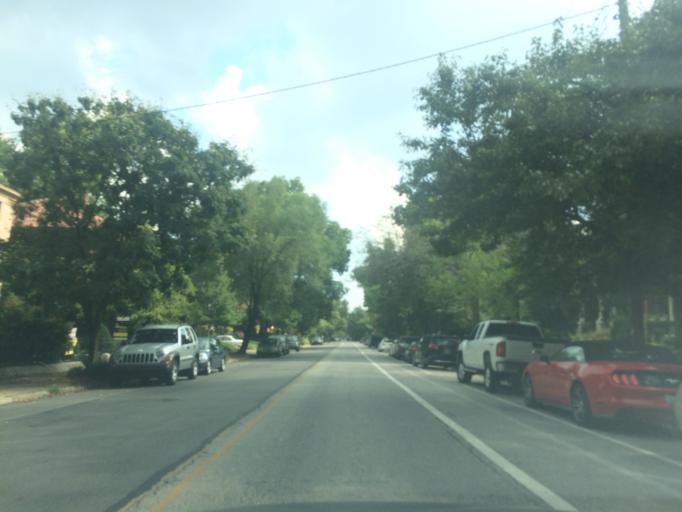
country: US
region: Kentucky
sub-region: Jefferson County
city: Louisville
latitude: 38.2305
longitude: -85.7560
